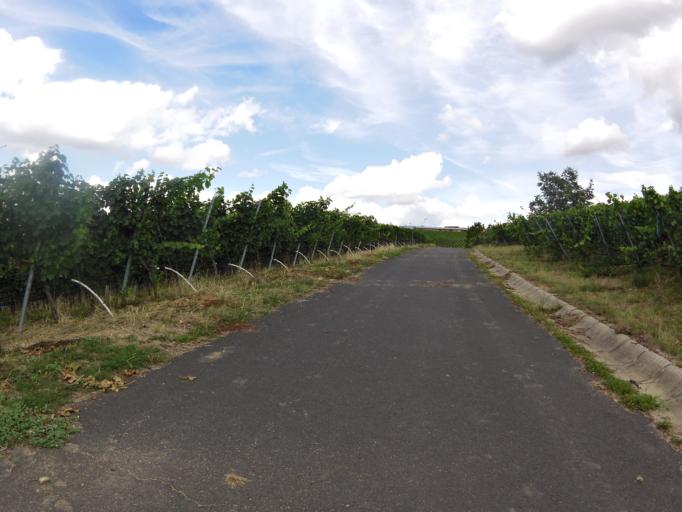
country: DE
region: Bavaria
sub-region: Regierungsbezirk Unterfranken
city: Sommerhausen
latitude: 49.6953
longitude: 10.0323
